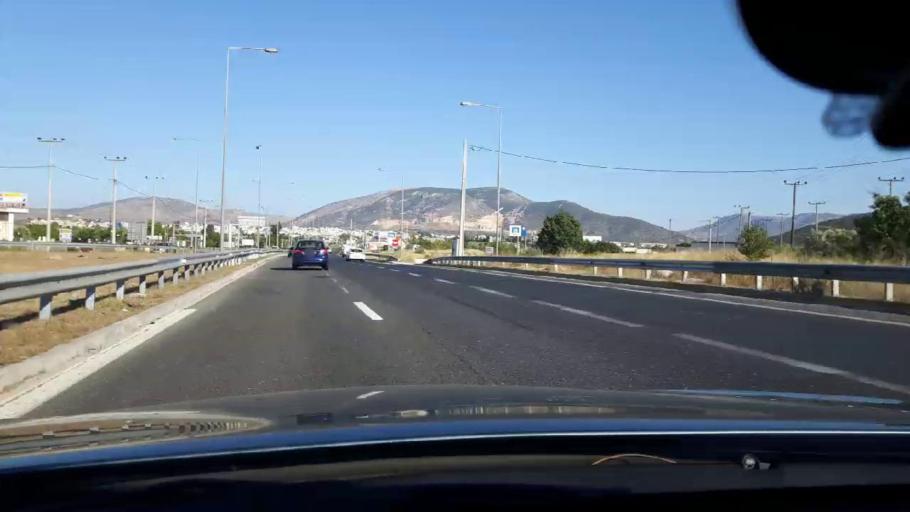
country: GR
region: Attica
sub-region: Nomarchia Anatolikis Attikis
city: Markopoulo
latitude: 37.8926
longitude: 23.9167
